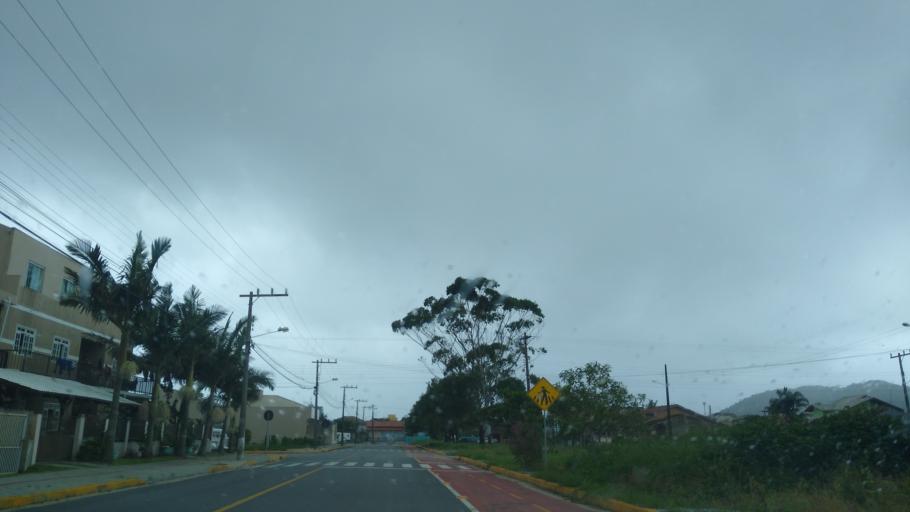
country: BR
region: Santa Catarina
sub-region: Sao Francisco Do Sul
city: Sao Francisco do Sul
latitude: -26.2342
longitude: -48.5110
